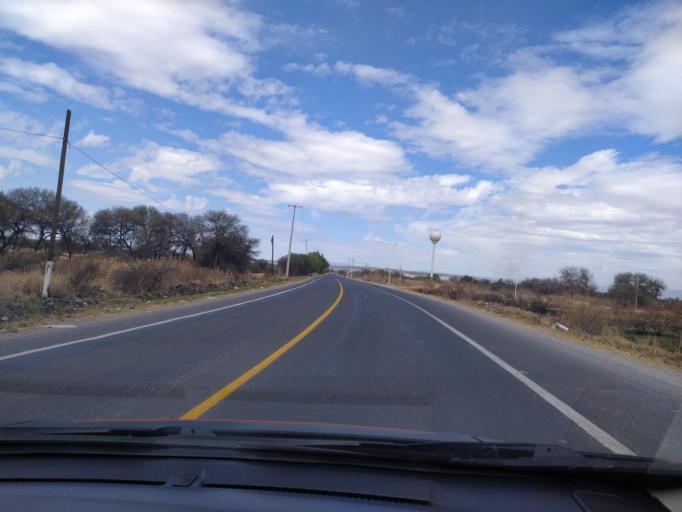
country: LA
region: Oudomxai
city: Muang La
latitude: 20.9943
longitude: 101.8340
